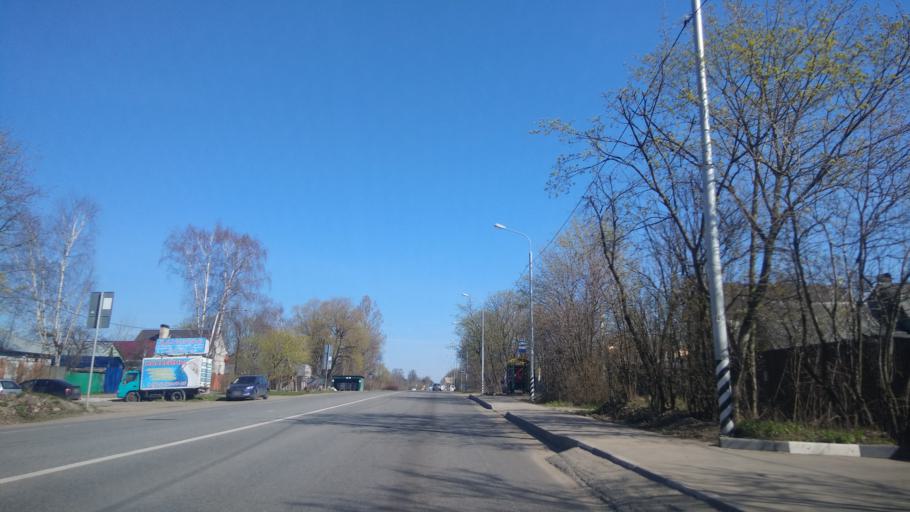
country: RU
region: Moskovskaya
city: Pushkino
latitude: 56.0154
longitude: 37.8719
